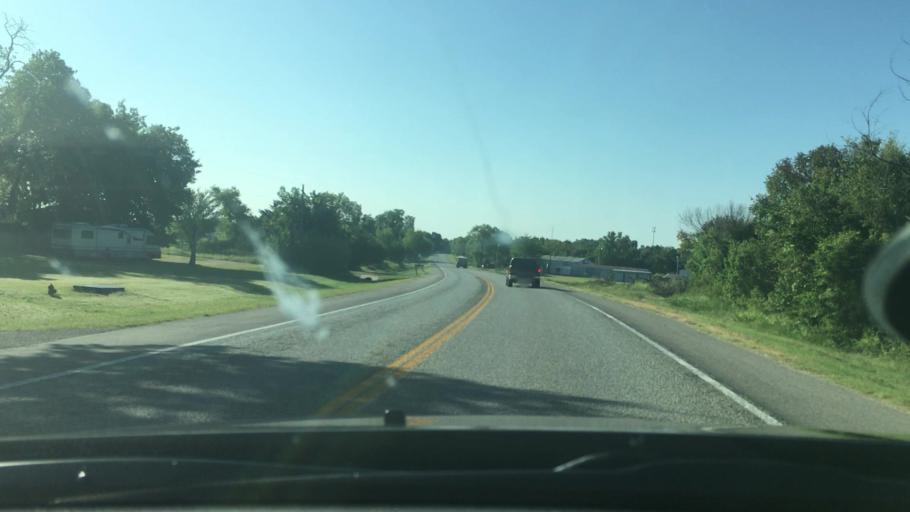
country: US
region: Oklahoma
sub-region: Johnston County
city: Tishomingo
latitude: 34.2488
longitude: -96.7583
